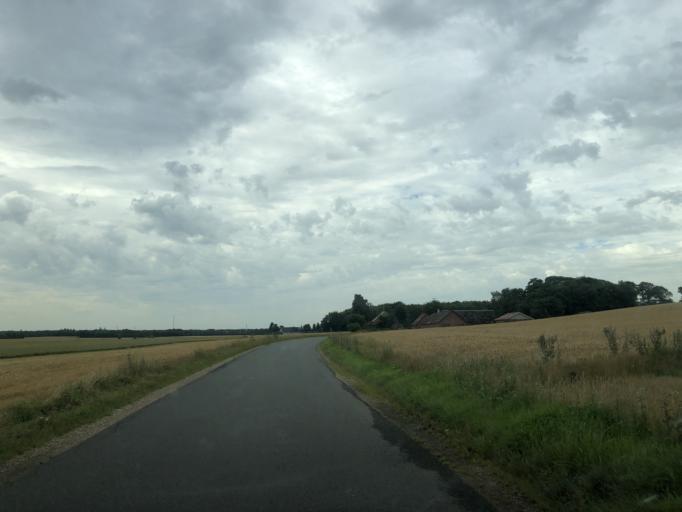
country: DK
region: Central Jutland
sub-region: Holstebro Kommune
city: Holstebro
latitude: 56.3876
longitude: 8.5241
